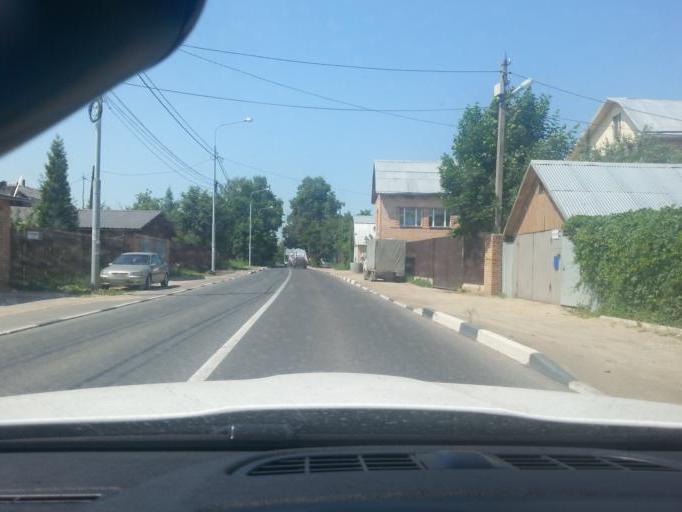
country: RU
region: Moskovskaya
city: Zheleznodorozhnyy
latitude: 55.7254
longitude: 38.0002
